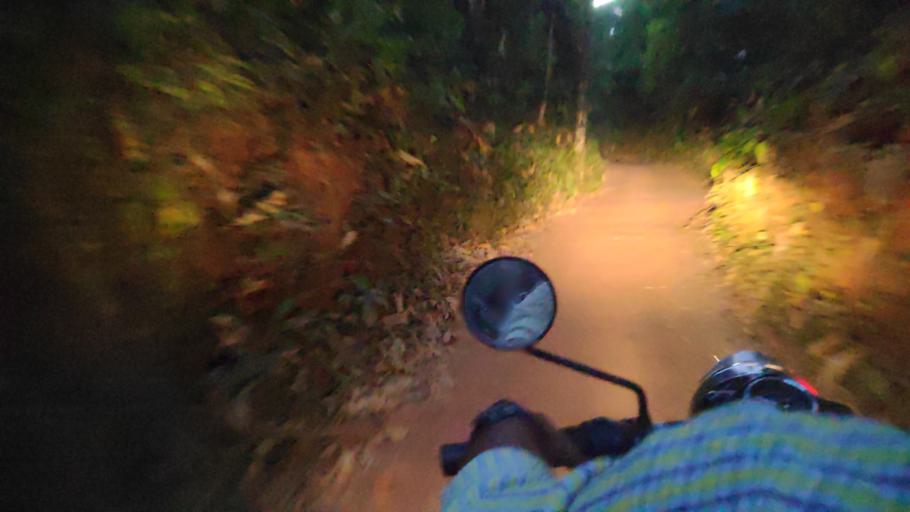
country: IN
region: Kerala
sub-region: Kozhikode
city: Kunnamangalam
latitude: 11.2806
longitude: 75.8286
